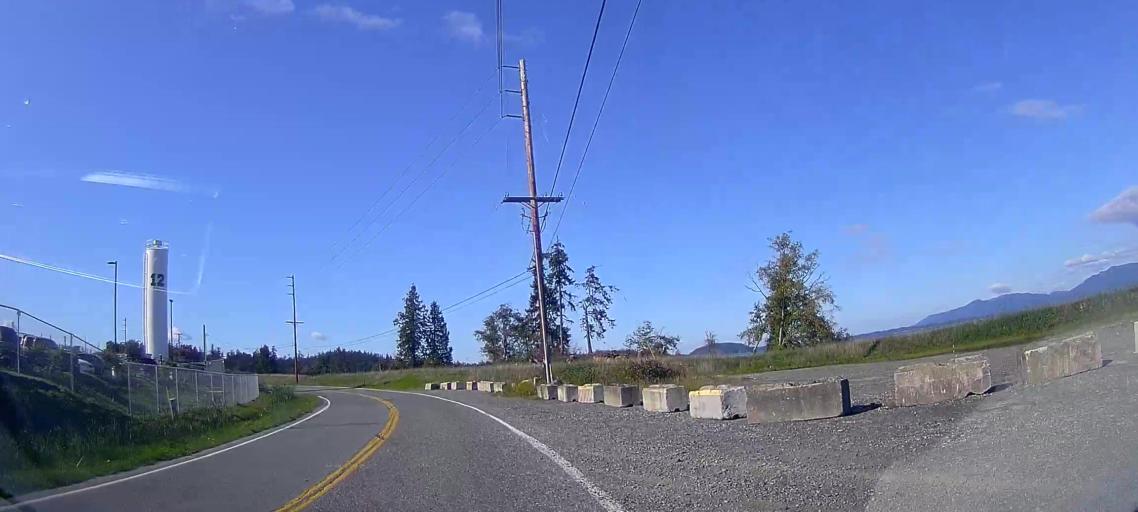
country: US
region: Washington
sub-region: Skagit County
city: Anacortes
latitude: 48.4649
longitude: -122.5336
